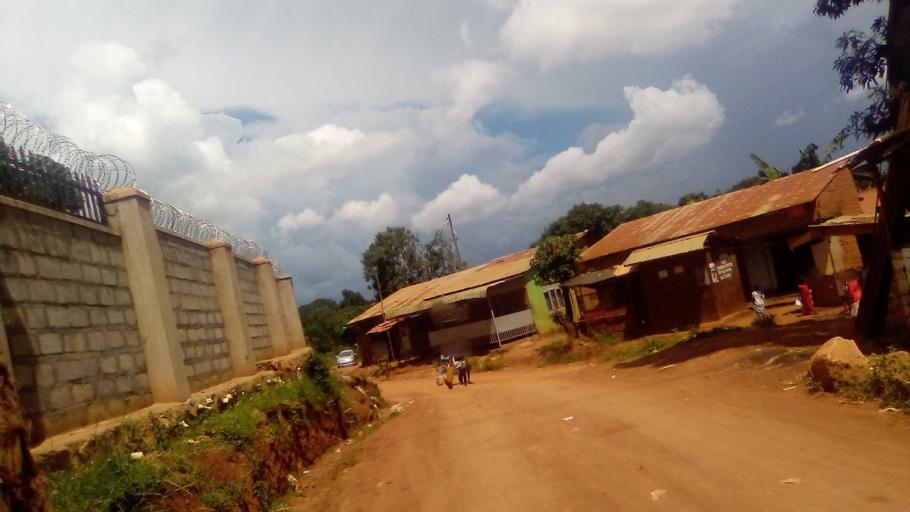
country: UG
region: Central Region
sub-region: Wakiso District
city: Entebbe
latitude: 0.0954
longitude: 32.5082
